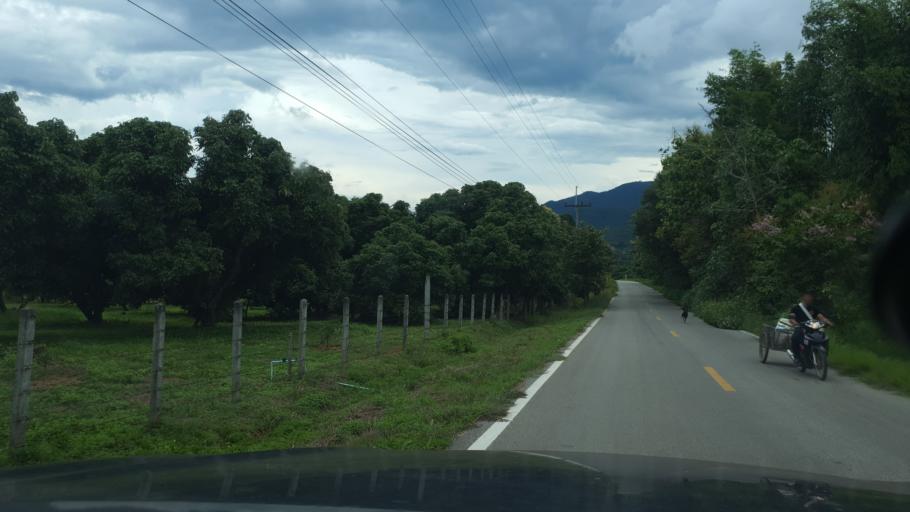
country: TH
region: Lamphun
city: Mae Tha
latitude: 18.5293
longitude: 99.2437
